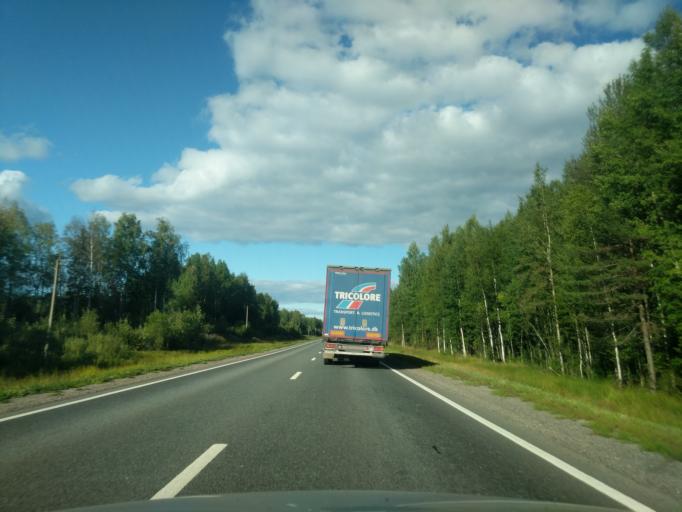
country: RU
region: Kostroma
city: Manturovo
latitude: 58.1479
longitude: 44.3689
